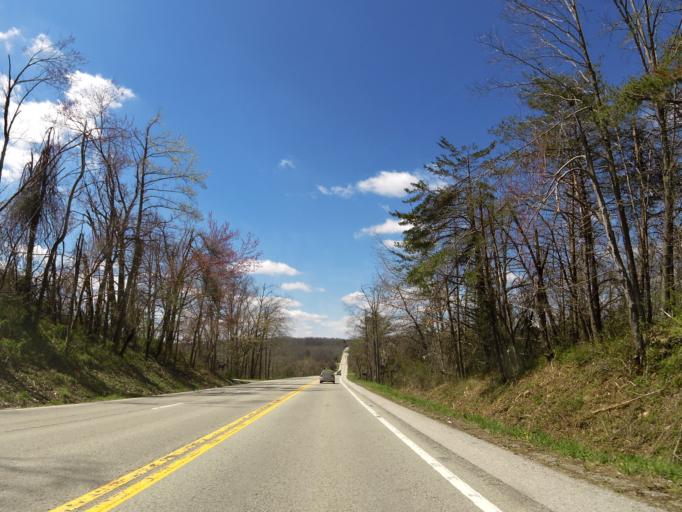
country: US
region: Tennessee
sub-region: Cumberland County
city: Crossville
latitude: 35.9722
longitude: -85.1905
